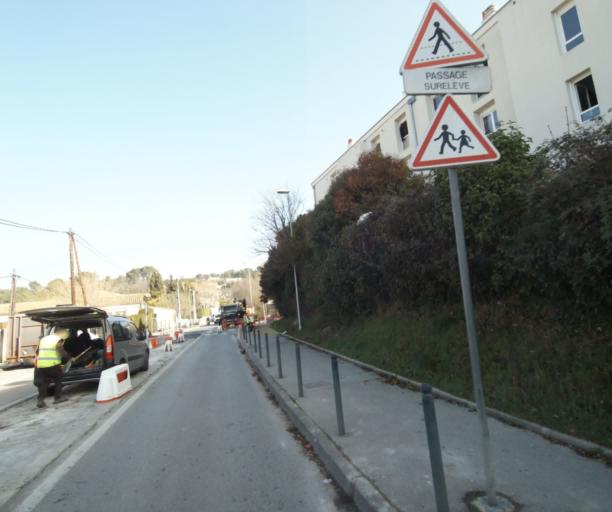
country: FR
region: Provence-Alpes-Cote d'Azur
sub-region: Departement des Bouches-du-Rhone
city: Aix-en-Provence
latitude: 43.5408
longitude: 5.4539
